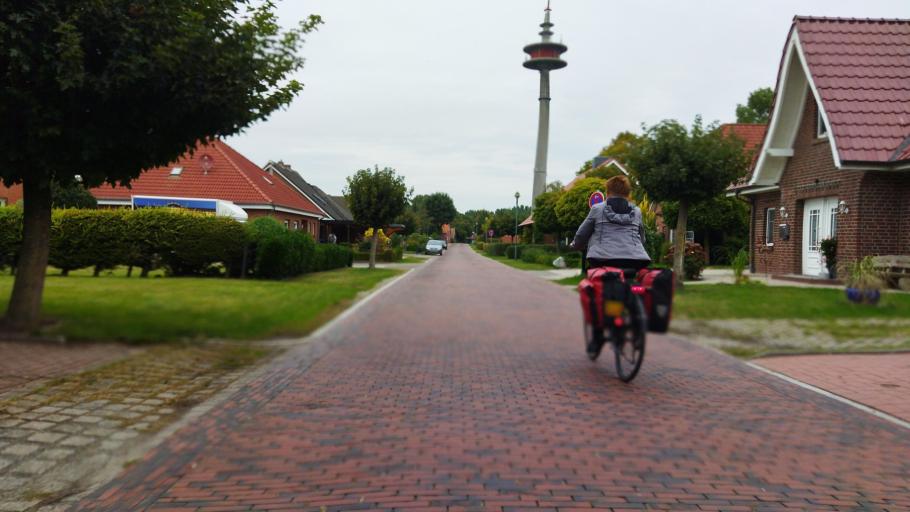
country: DE
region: Lower Saxony
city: Leer
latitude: 53.2607
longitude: 7.4352
